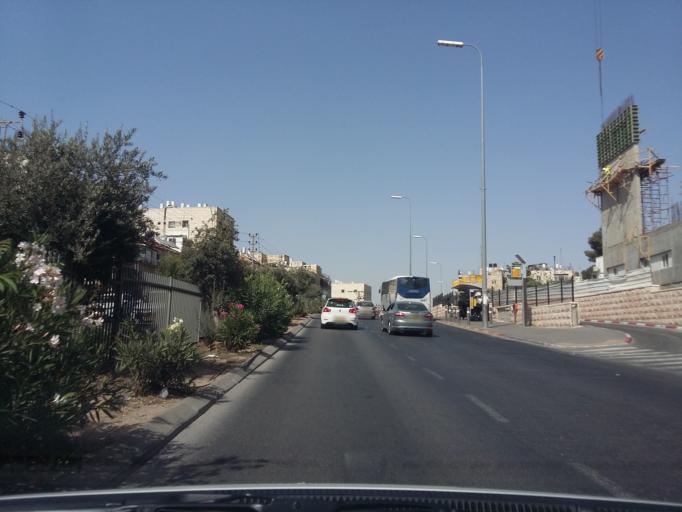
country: IL
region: Jerusalem
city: West Jerusalem
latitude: 31.7929
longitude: 35.2136
